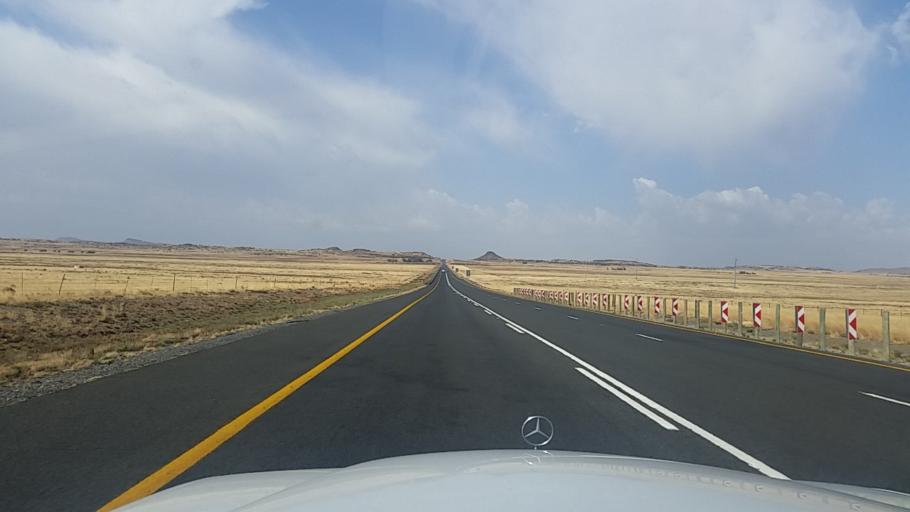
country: ZA
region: Orange Free State
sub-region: Xhariep District Municipality
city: Trompsburg
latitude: -30.3151
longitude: 25.7107
